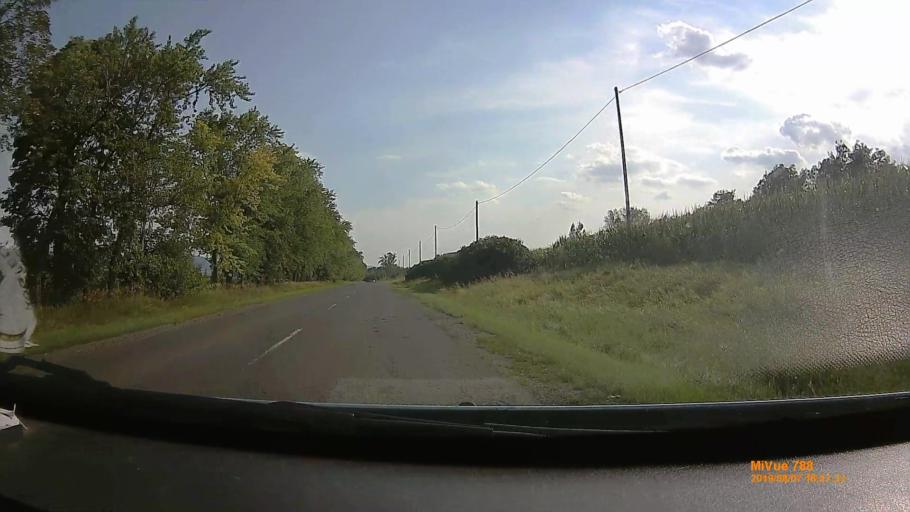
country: HU
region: Borsod-Abauj-Zemplen
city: Abaujszanto
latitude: 48.3405
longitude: 21.2072
